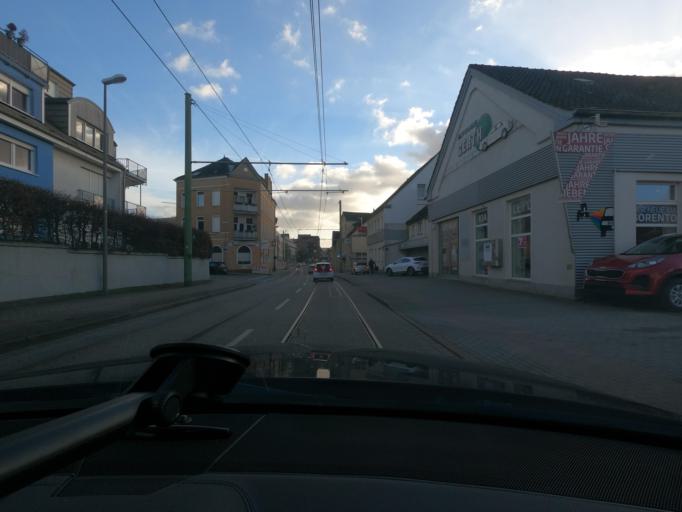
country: DE
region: North Rhine-Westphalia
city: Schwerte
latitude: 51.4963
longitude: 7.5549
